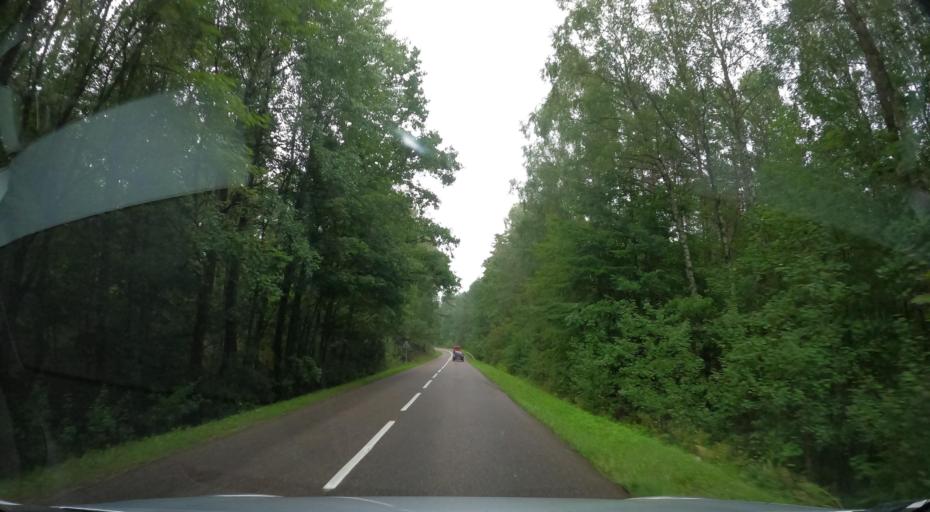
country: PL
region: Pomeranian Voivodeship
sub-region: Powiat wejherowski
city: Luzino
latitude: 54.4769
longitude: 18.0926
